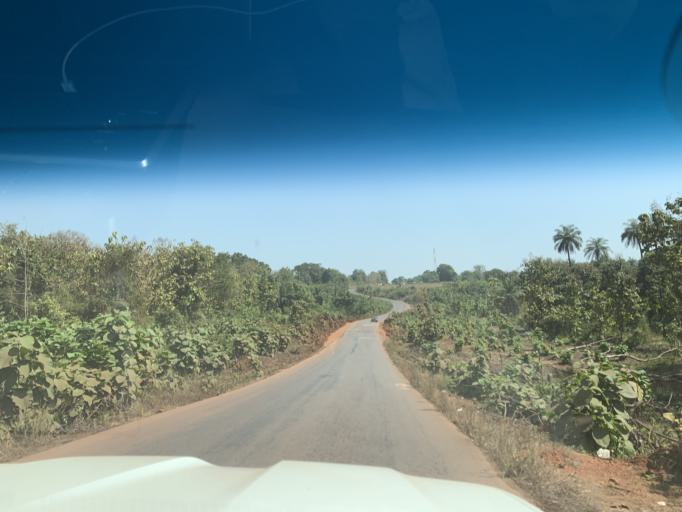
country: GN
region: Kindia
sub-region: Kindia
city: Kindia
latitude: 9.9927
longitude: -12.7392
